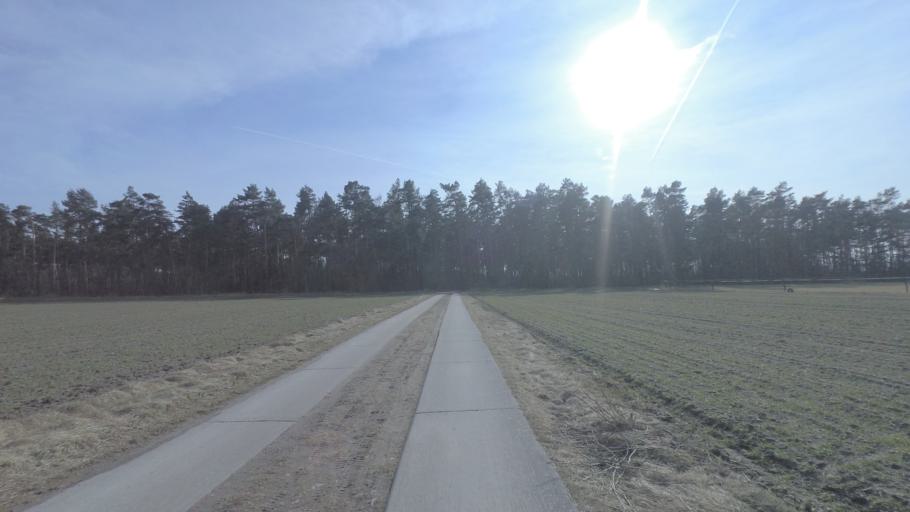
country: DE
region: Brandenburg
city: Ludwigsfelde
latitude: 52.2851
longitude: 13.2754
